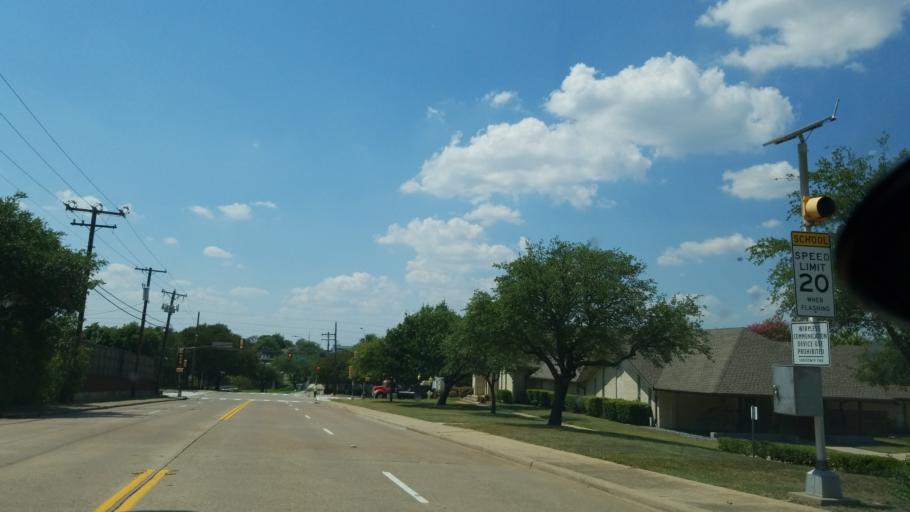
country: US
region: Texas
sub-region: Dallas County
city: Richardson
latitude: 32.8860
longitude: -96.7168
